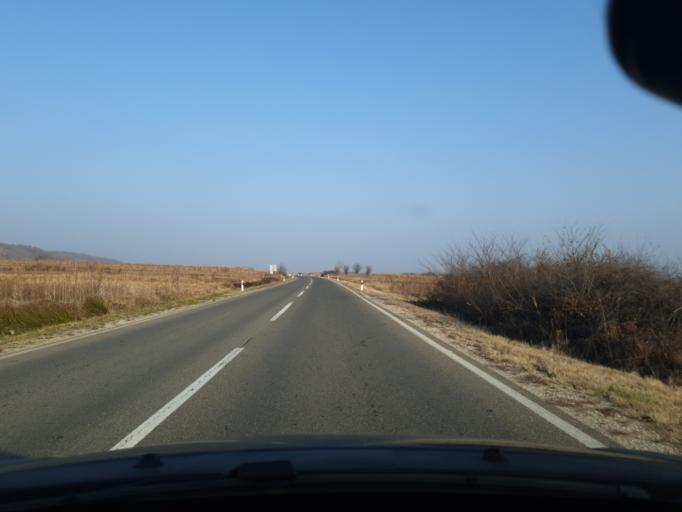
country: RS
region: Central Serbia
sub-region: Jablanicki Okrug
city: Leskovac
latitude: 42.9486
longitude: 21.9914
